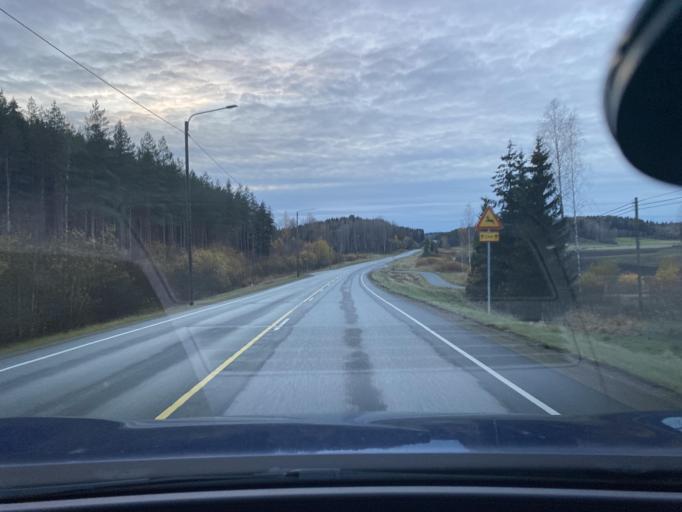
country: FI
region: Uusimaa
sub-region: Helsinki
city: Saukkola
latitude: 60.3853
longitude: 24.0692
